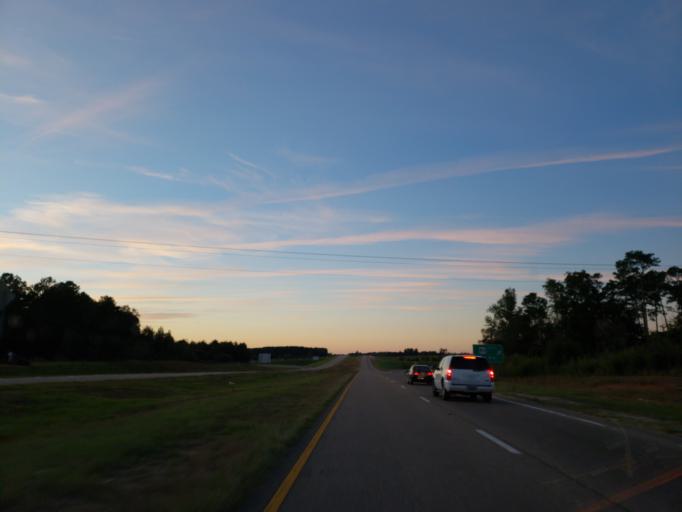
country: US
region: Mississippi
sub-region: Wayne County
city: Waynesboro
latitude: 31.7024
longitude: -88.6220
